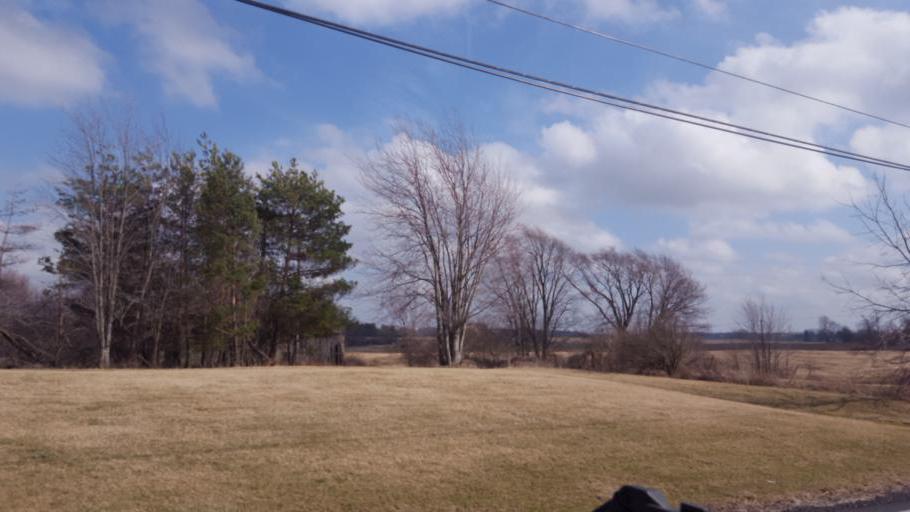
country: US
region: Ohio
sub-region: Richland County
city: Shelby
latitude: 40.8446
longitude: -82.6603
